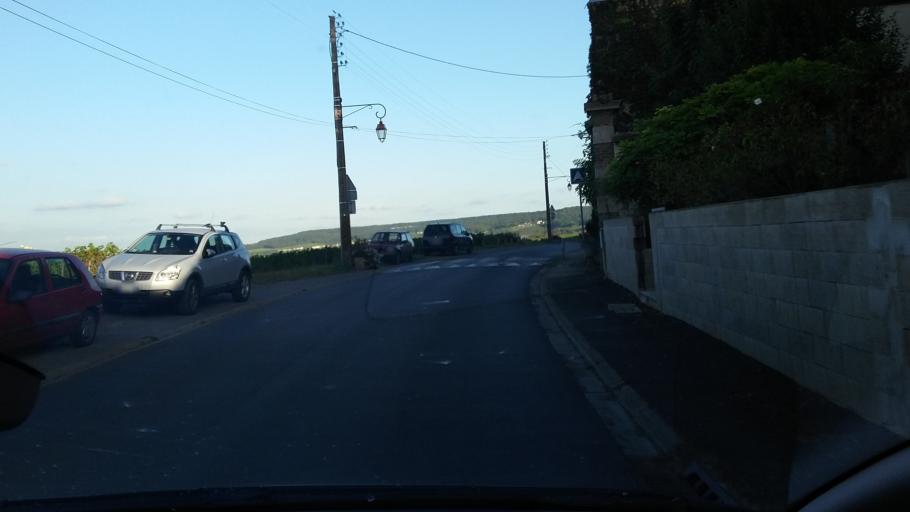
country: FR
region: Champagne-Ardenne
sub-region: Departement de la Marne
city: Rilly-la-Montagne
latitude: 49.1635
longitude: 4.0494
